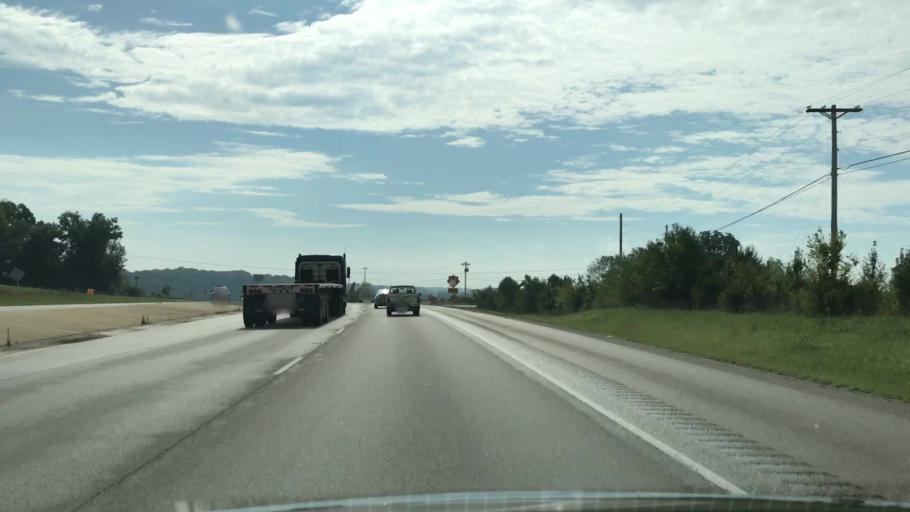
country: US
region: Kentucky
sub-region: Warren County
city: Plano
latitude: 36.9030
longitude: -86.3965
